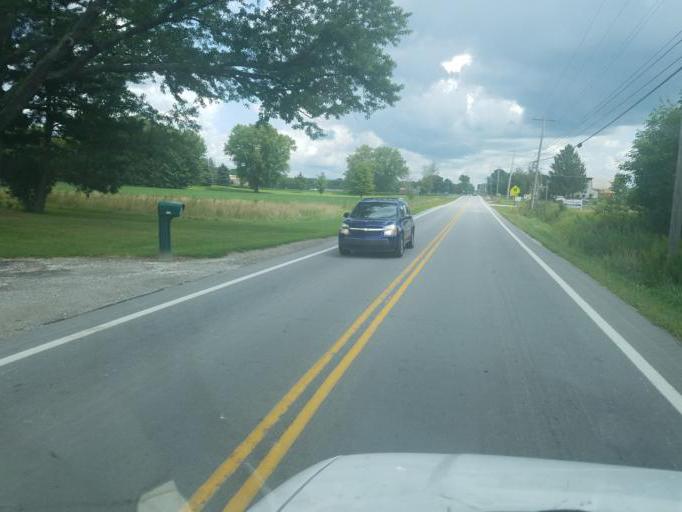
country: US
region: Ohio
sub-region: Ashtabula County
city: Andover
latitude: 41.6070
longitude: -80.5937
